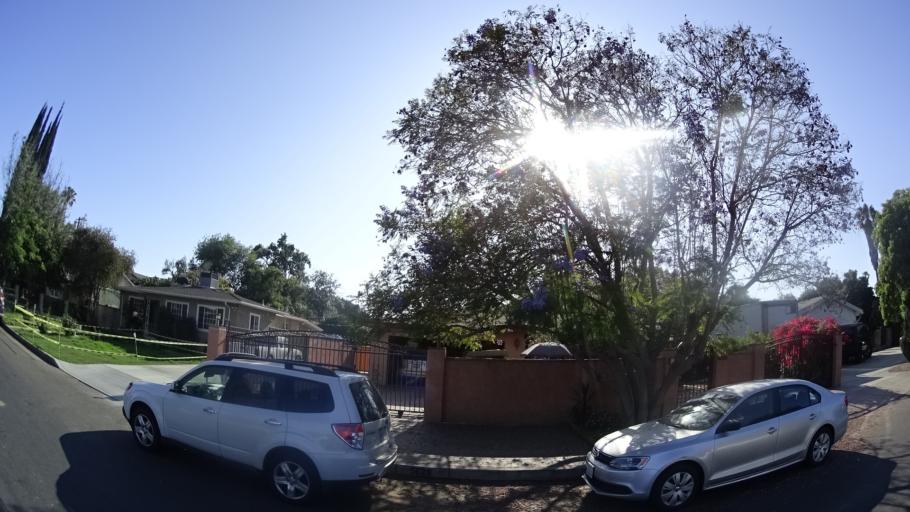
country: US
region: California
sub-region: Los Angeles County
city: Van Nuys
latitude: 34.1729
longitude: -118.4422
